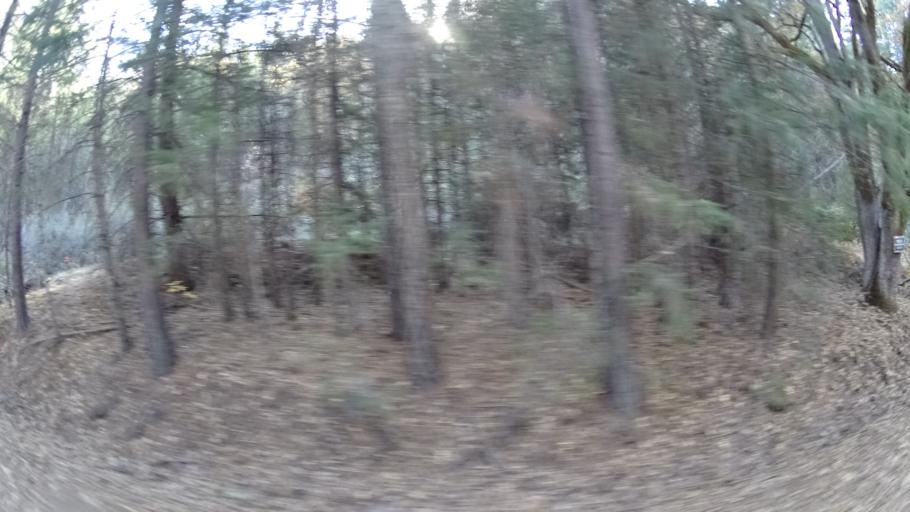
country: US
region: California
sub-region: Siskiyou County
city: Yreka
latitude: 41.8302
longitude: -122.9567
